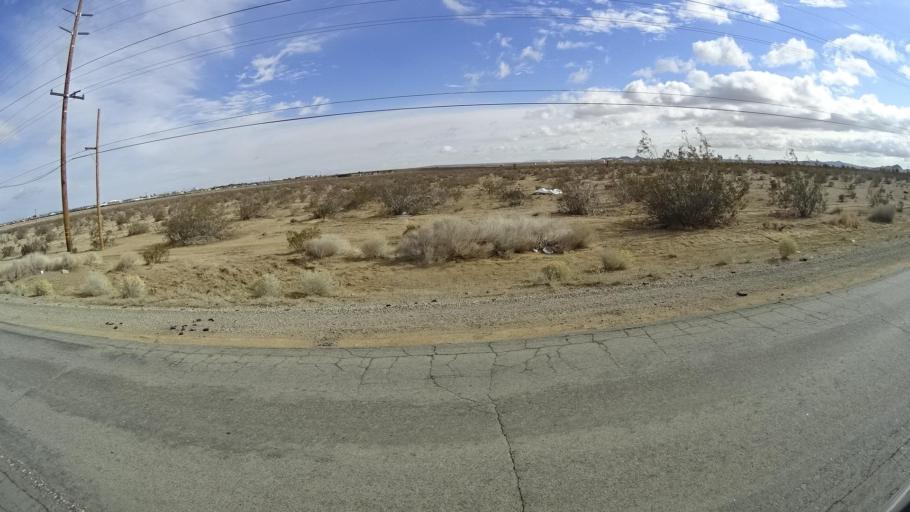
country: US
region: California
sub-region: Kern County
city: Mojave
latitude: 35.0364
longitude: -118.1855
